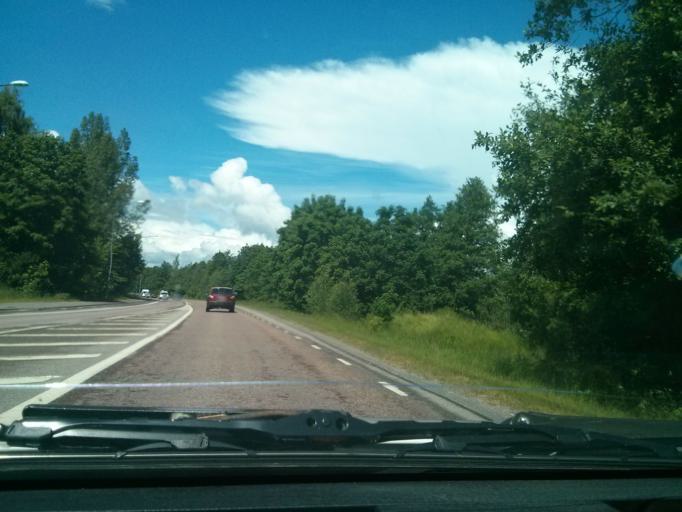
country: SE
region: Soedermanland
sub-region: Nykopings Kommun
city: Nykoping
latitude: 58.7733
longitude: 16.9833
